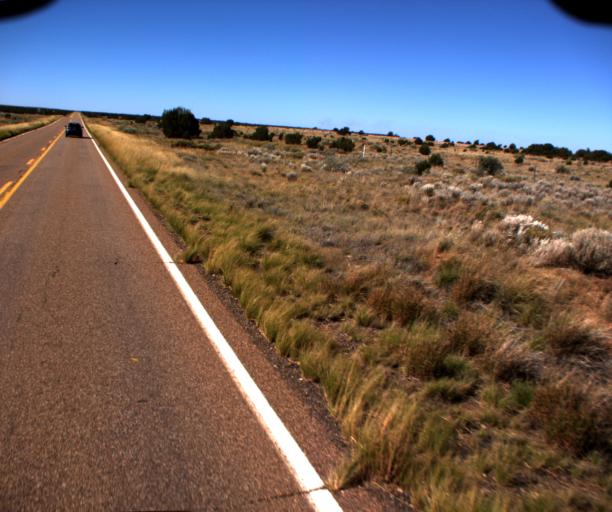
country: US
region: Arizona
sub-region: Navajo County
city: Heber-Overgaard
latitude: 34.4740
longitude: -110.3545
